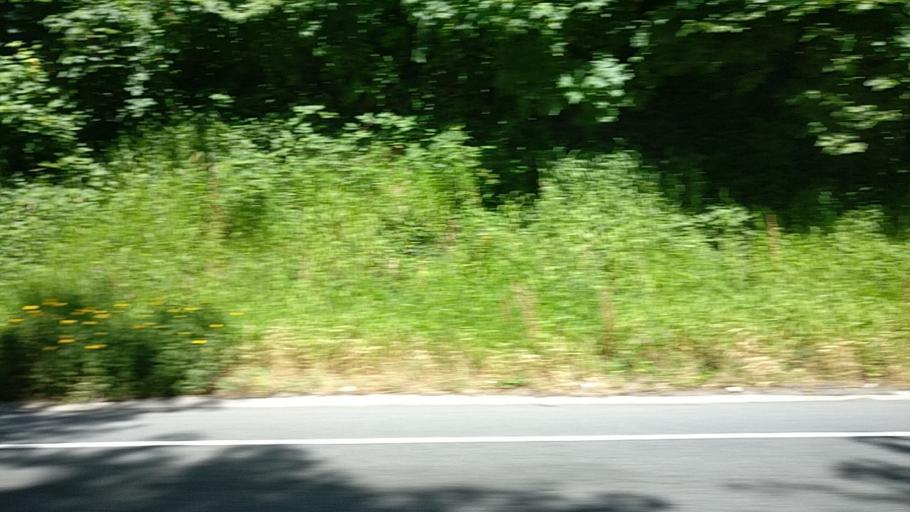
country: CA
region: British Columbia
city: Langley
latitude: 49.0311
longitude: -122.6666
